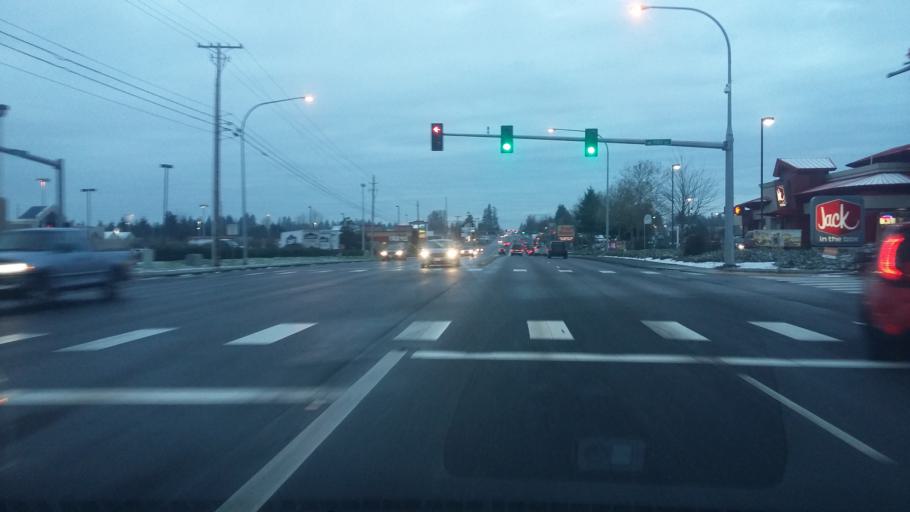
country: US
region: Washington
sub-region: Clark County
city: Orchards
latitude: 45.6743
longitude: -122.5526
